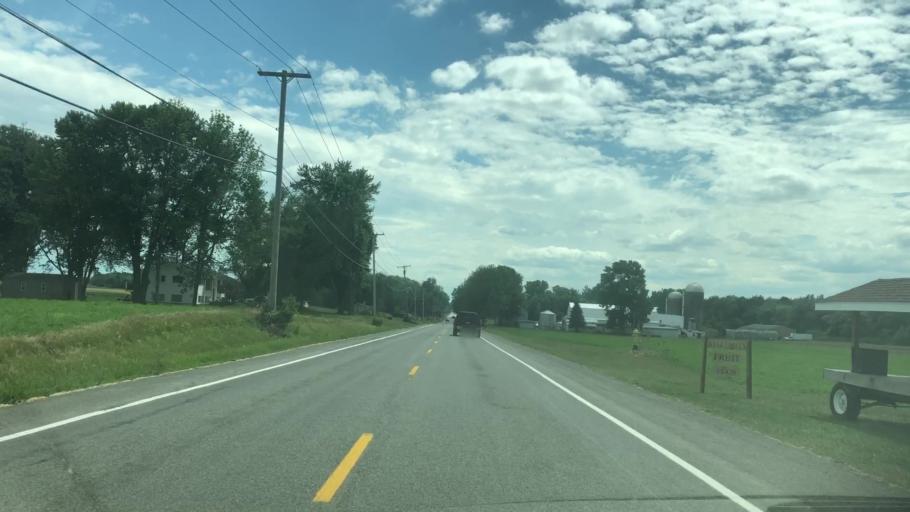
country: US
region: New York
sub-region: Monroe County
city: Fairport
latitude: 43.1508
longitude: -77.4006
